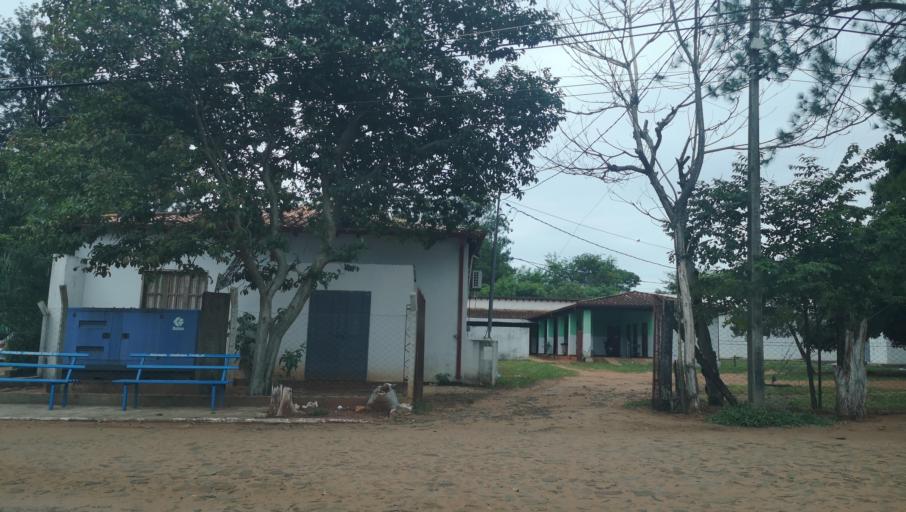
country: PY
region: San Pedro
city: Capiibary
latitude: -24.7276
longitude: -56.0172
